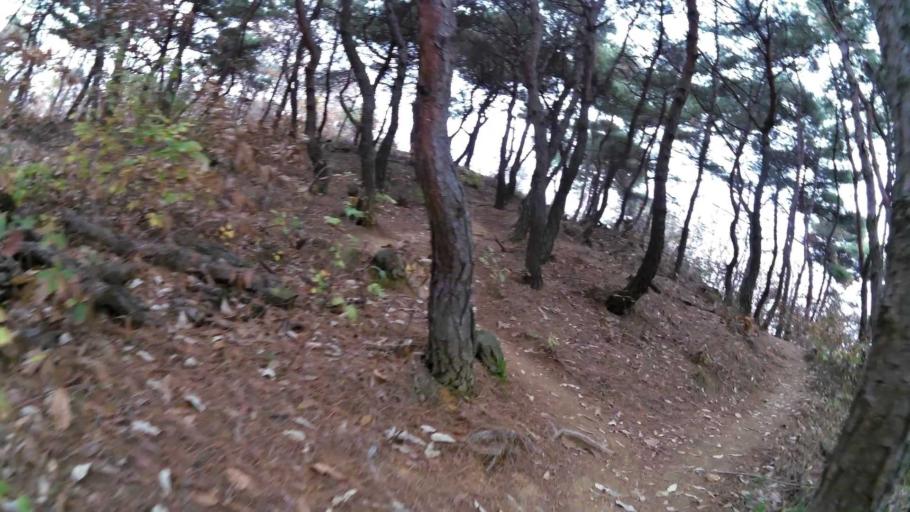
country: KR
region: Daegu
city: Daegu
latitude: 35.8611
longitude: 128.6619
